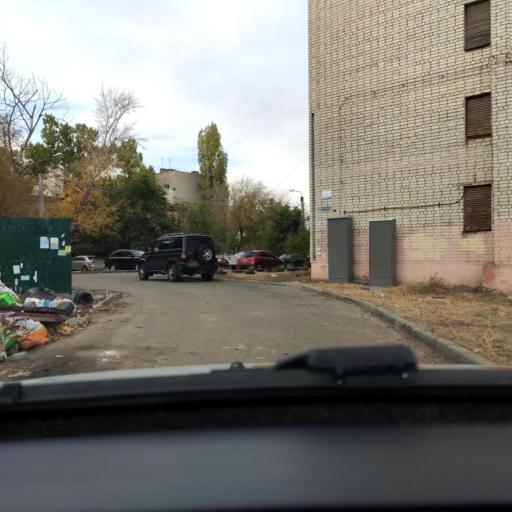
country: RU
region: Voronezj
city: Maslovka
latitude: 51.6187
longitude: 39.2528
